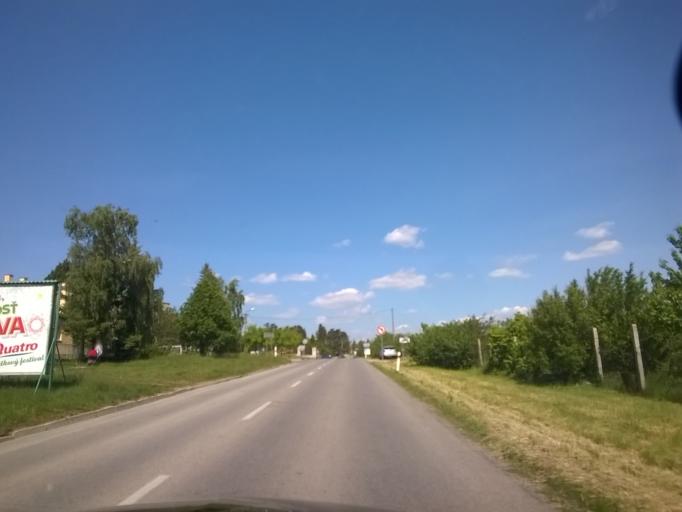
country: SK
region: Nitriansky
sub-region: Okres Nitra
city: Nitra
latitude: 48.3276
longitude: 18.1147
